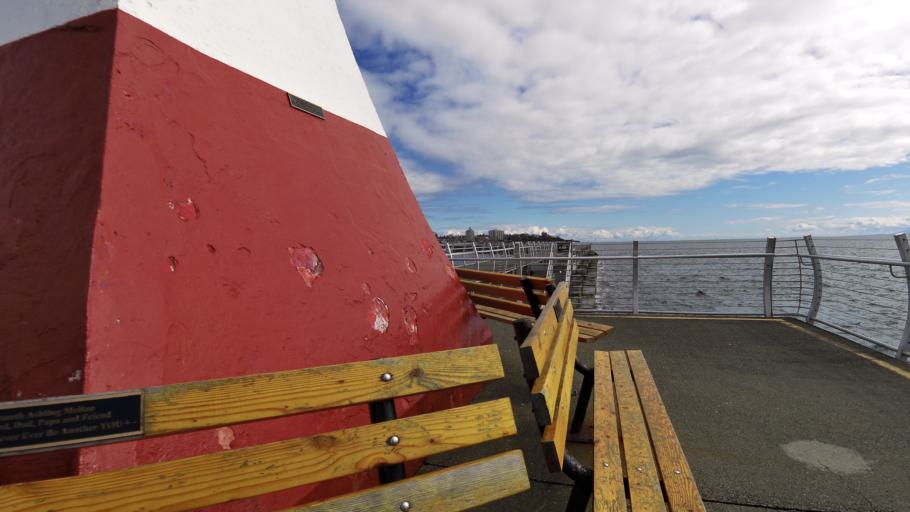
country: CA
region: British Columbia
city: Victoria
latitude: 48.4135
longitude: -123.3939
